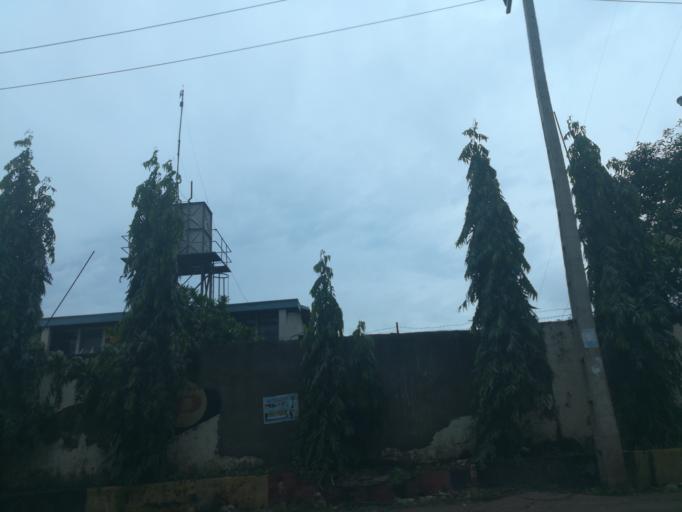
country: NG
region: Lagos
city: Agege
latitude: 6.6141
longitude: 3.3350
